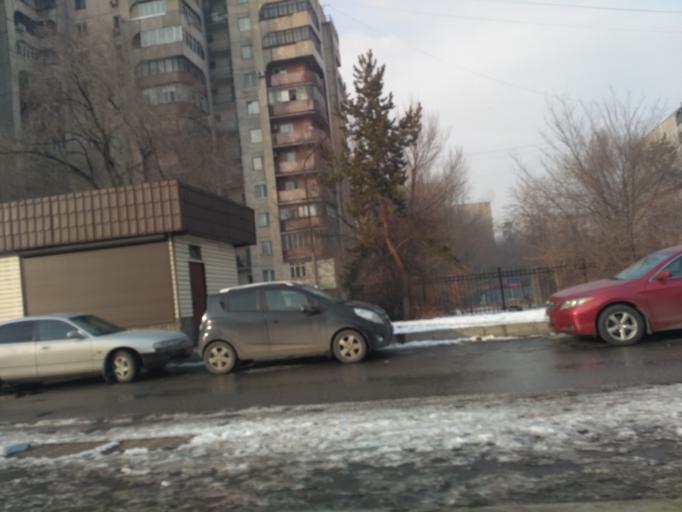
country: KZ
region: Almaty Qalasy
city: Almaty
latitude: 43.2404
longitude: 76.8340
